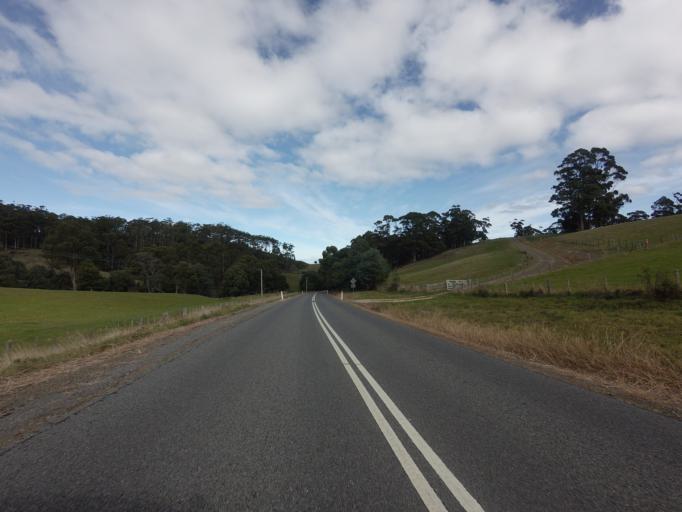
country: AU
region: Tasmania
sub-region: Clarence
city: Sandford
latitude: -43.0764
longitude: 147.7488
